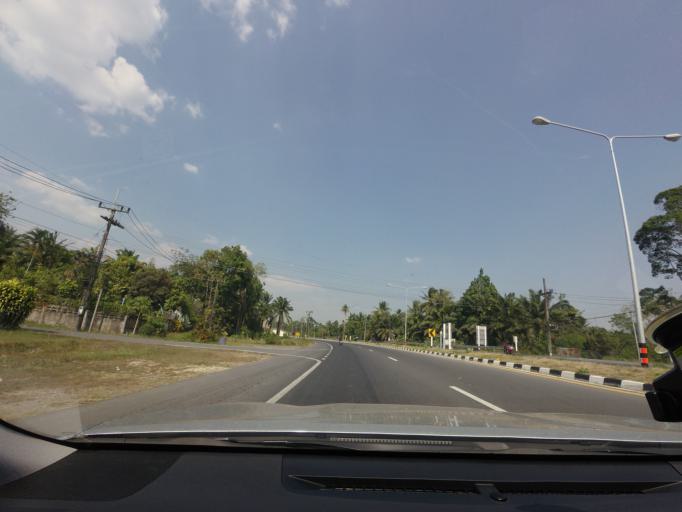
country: TH
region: Phangnga
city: Thap Put
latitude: 8.5423
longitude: 98.7243
